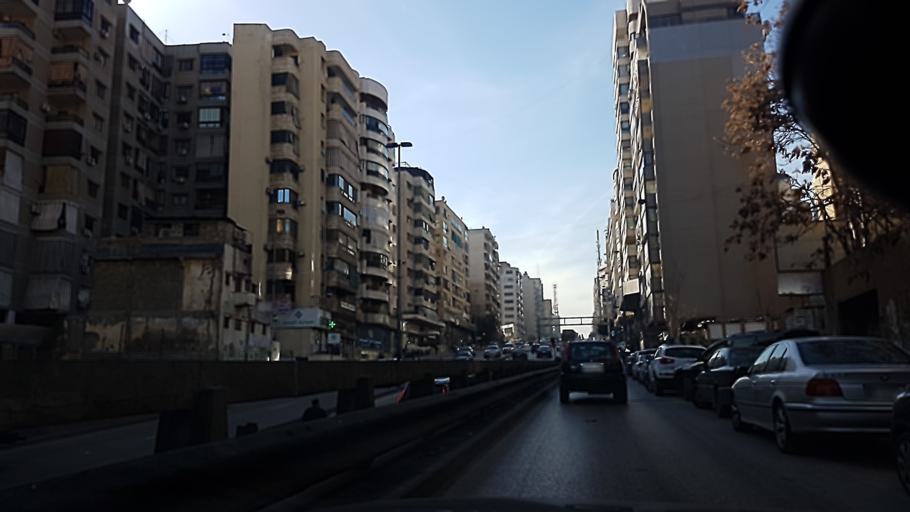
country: LB
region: Beyrouth
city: Beirut
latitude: 33.8911
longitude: 35.5006
